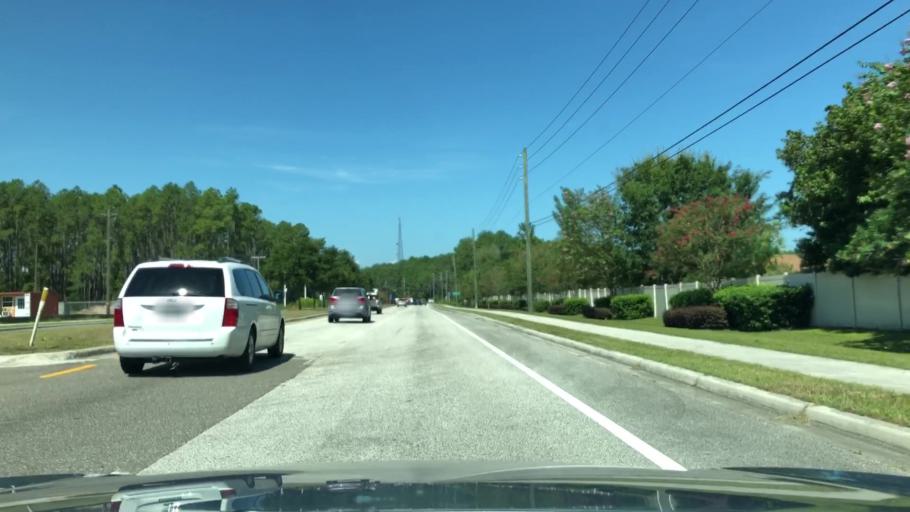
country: US
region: Florida
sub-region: Saint Johns County
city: Fruit Cove
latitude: 30.0600
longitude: -81.5268
